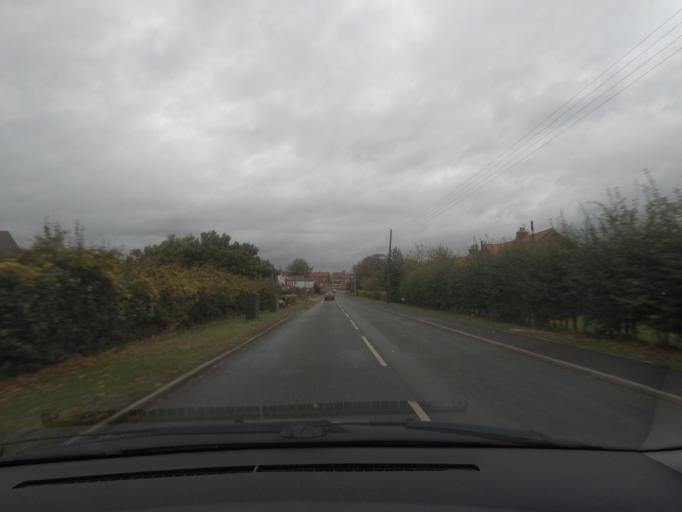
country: GB
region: England
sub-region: North Yorkshire
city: Easingwold
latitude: 54.1011
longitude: -1.1108
